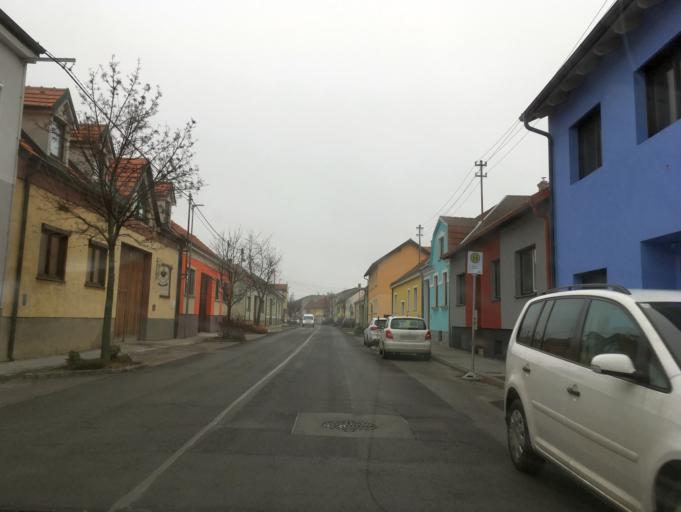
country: AT
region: Lower Austria
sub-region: Politischer Bezirk Bruck an der Leitha
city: Trautmannsdorf an der Leitha
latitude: 48.0547
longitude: 16.6397
